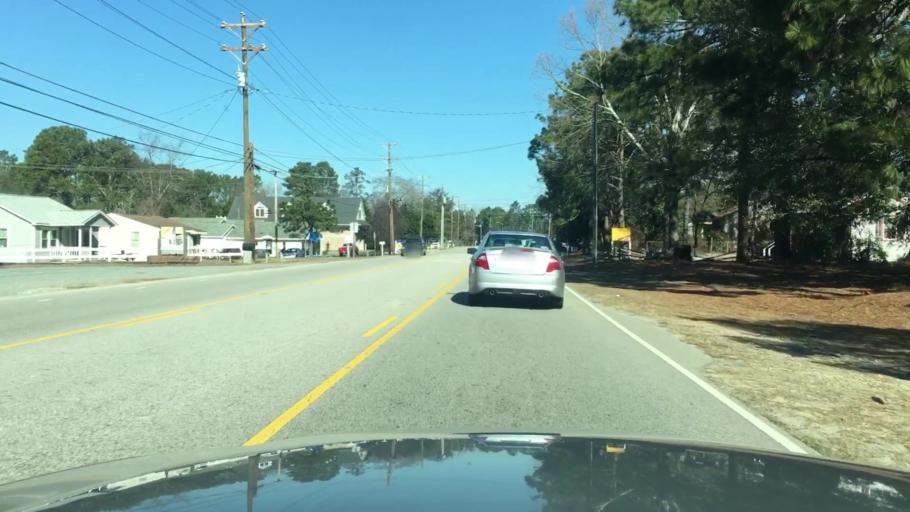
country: US
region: North Carolina
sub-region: Cumberland County
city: Hope Mills
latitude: 35.0168
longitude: -78.9351
